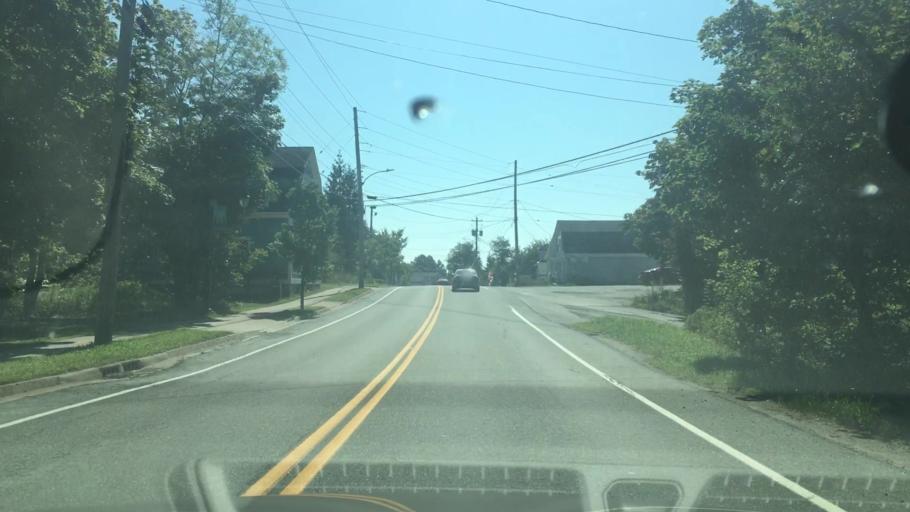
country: CA
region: Nova Scotia
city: New Glasgow
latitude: 44.9261
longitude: -62.5416
